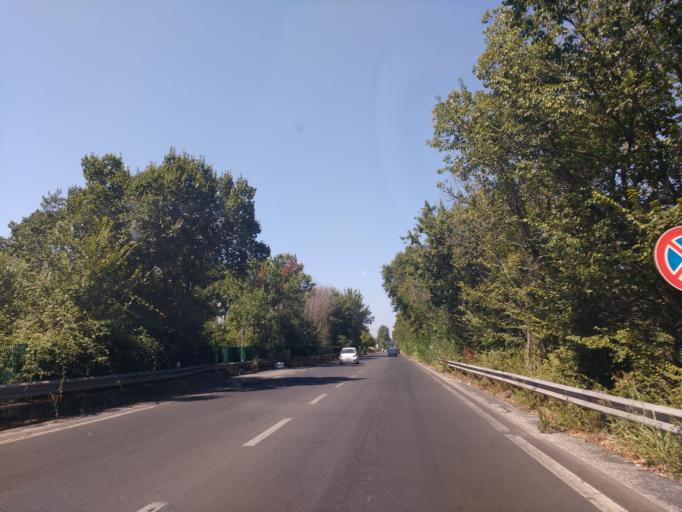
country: IT
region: Latium
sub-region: Citta metropolitana di Roma Capitale
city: Acilia-Castel Fusano-Ostia Antica
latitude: 41.7718
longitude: 12.3300
